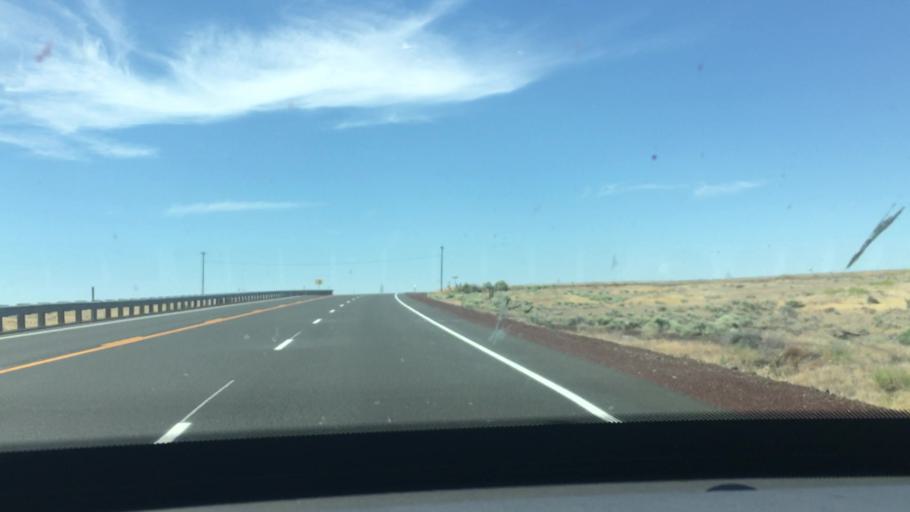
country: US
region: Oregon
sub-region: Sherman County
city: Moro
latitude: 45.2707
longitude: -120.7472
